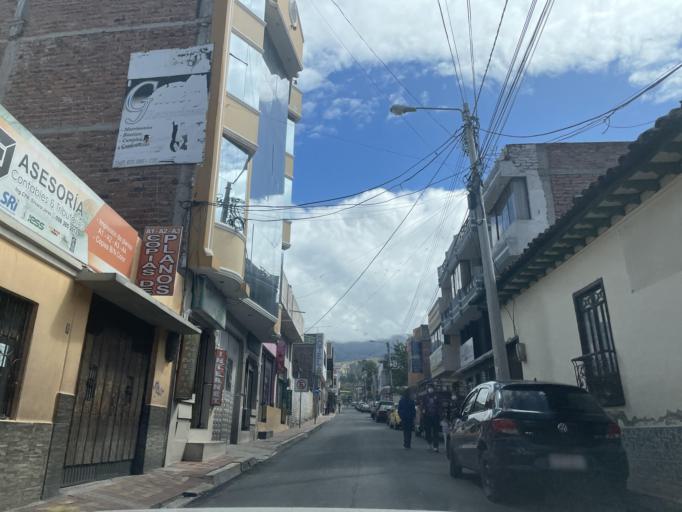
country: EC
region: Chimborazo
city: Guano
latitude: -1.6072
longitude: -78.6453
